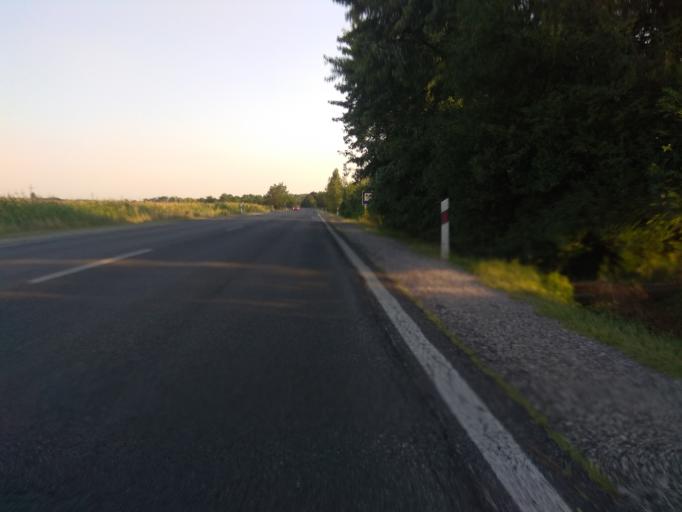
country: HU
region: Borsod-Abauj-Zemplen
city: Nyekladhaza
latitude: 47.9801
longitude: 20.8306
